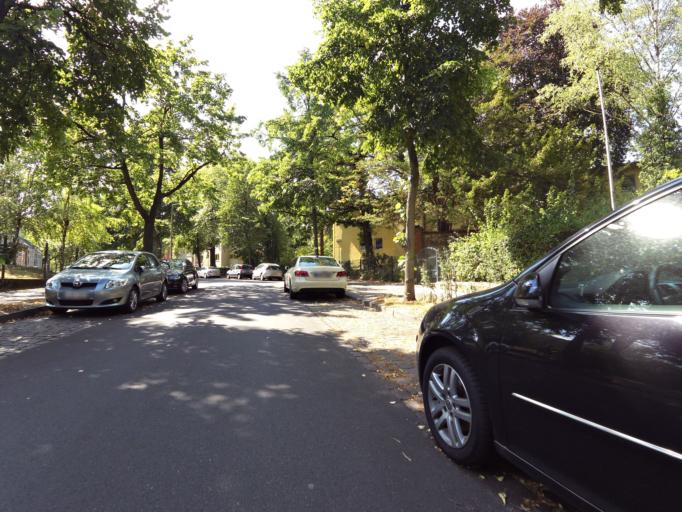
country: DE
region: Berlin
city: Schoneberg Bezirk
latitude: 52.4512
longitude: 13.3501
